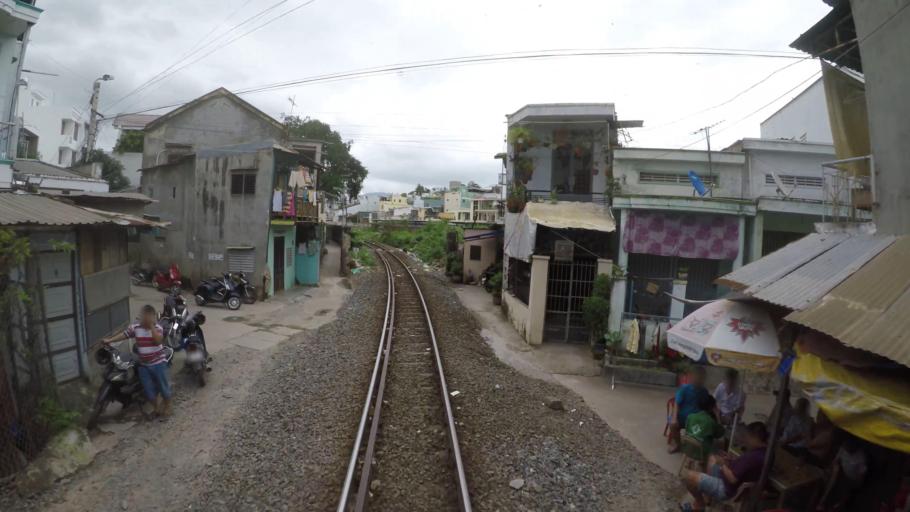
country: VN
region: Khanh Hoa
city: Nha Trang
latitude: 12.2482
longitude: 109.1834
